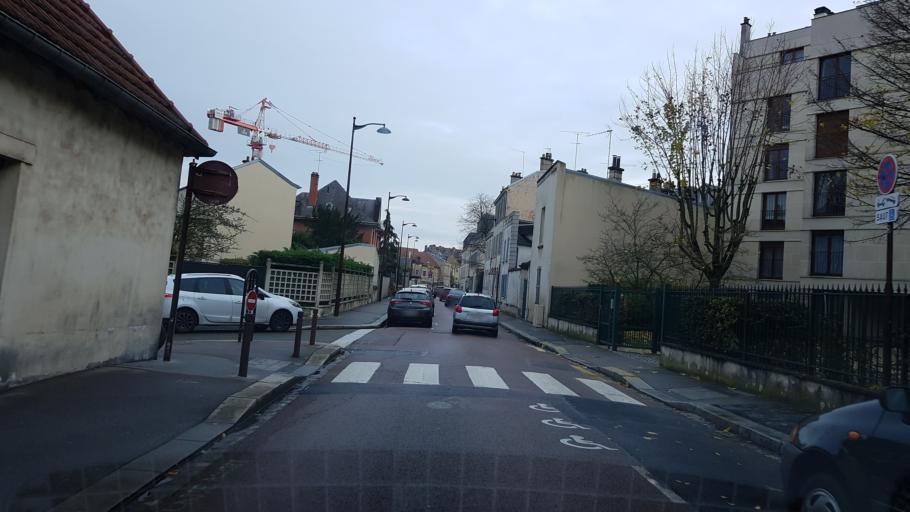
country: FR
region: Ile-de-France
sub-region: Departement des Yvelines
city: Versailles
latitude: 48.8049
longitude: 2.1424
